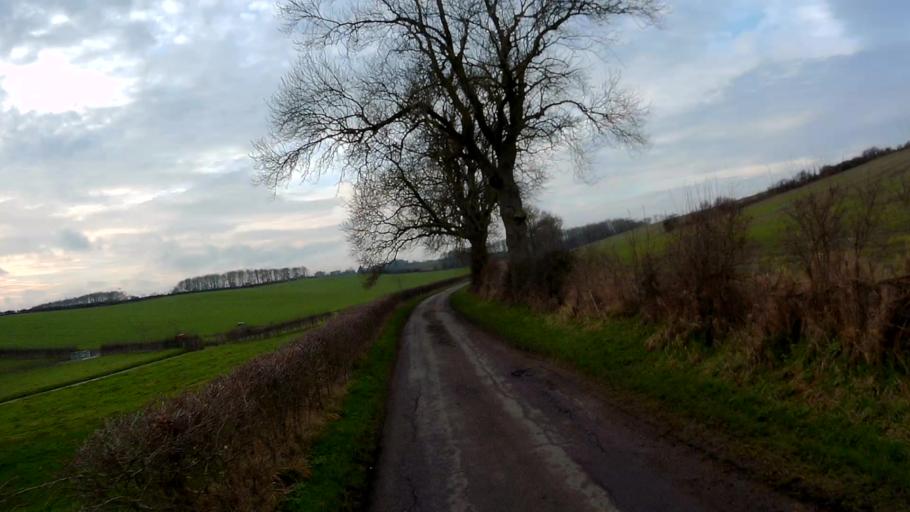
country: GB
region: England
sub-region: Lincolnshire
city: Bourne
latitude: 52.8281
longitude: -0.4645
